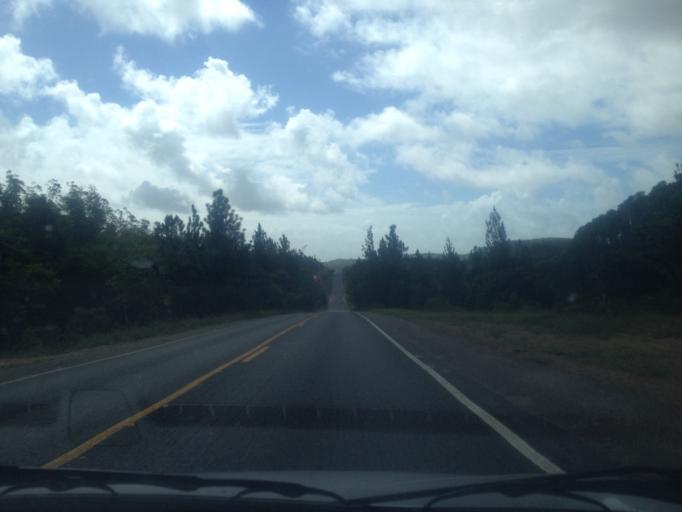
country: BR
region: Bahia
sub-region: Conde
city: Conde
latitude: -12.0014
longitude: -37.6833
